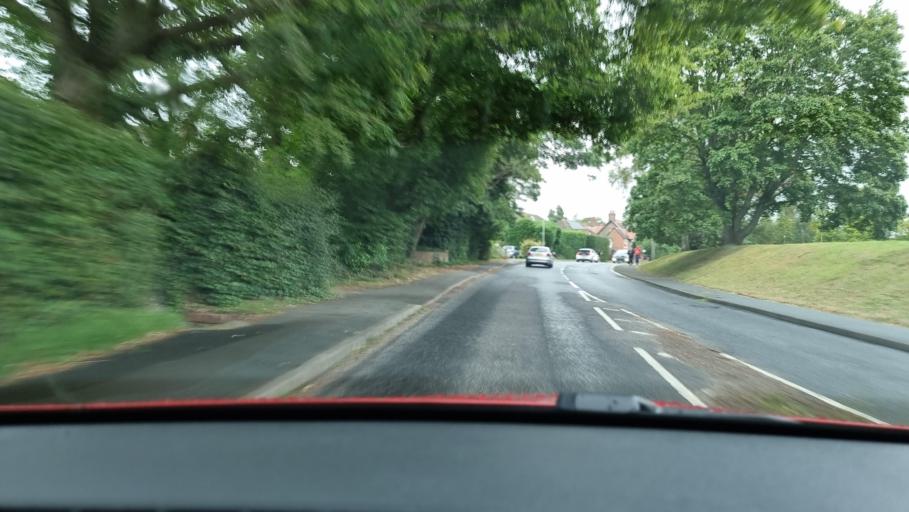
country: GB
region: England
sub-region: Buckinghamshire
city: Chesham
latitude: 51.7089
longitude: -0.6027
